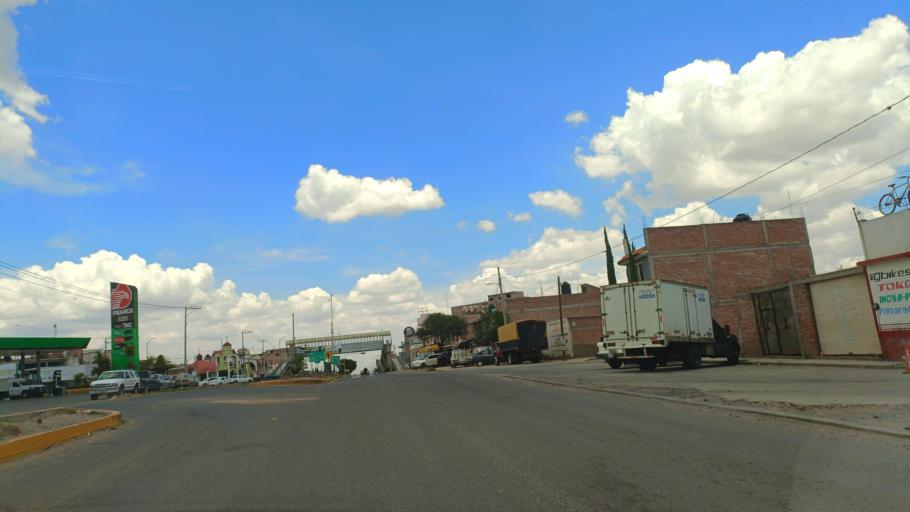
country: MX
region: Guerrero
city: San Luis de la Paz
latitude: 21.2889
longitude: -100.5090
